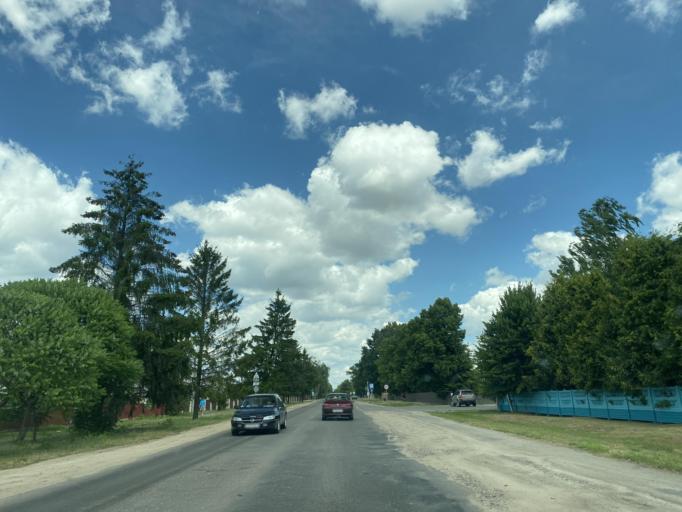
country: BY
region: Brest
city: Ivanava
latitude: 52.1591
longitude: 25.5456
